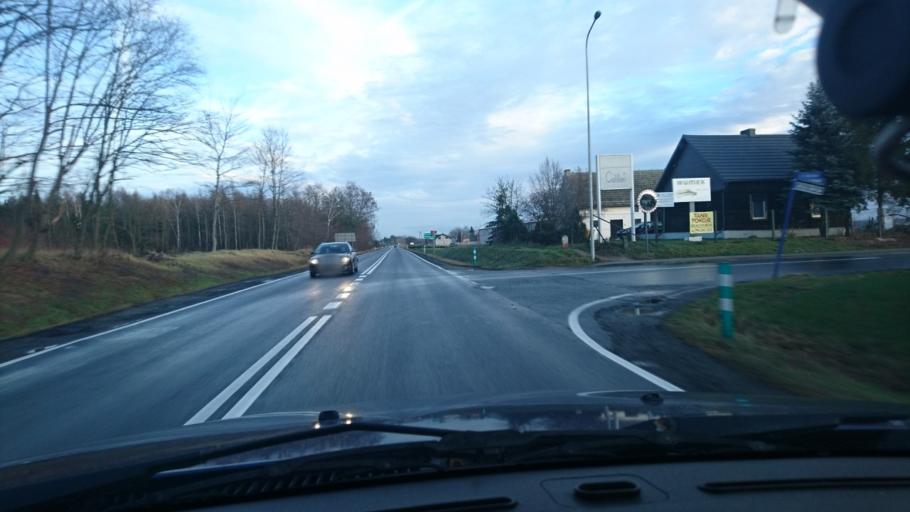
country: PL
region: Greater Poland Voivodeship
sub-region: Powiat kepinski
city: Leka Opatowska
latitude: 51.2249
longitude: 18.0953
